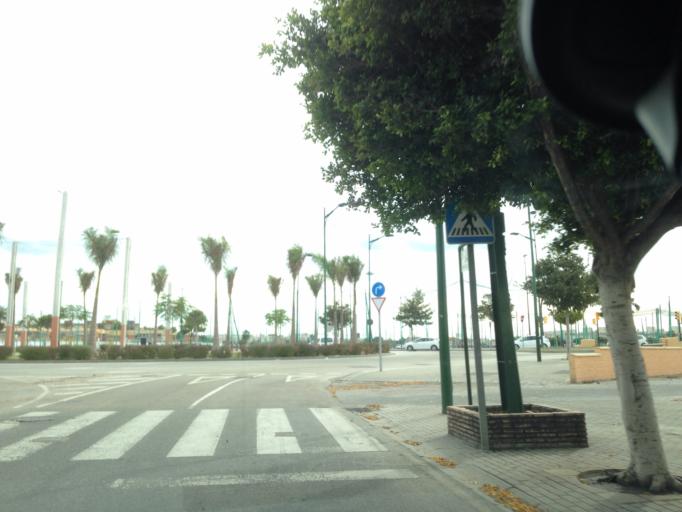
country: ES
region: Andalusia
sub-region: Provincia de Malaga
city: Malaga
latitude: 36.7017
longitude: -4.4623
